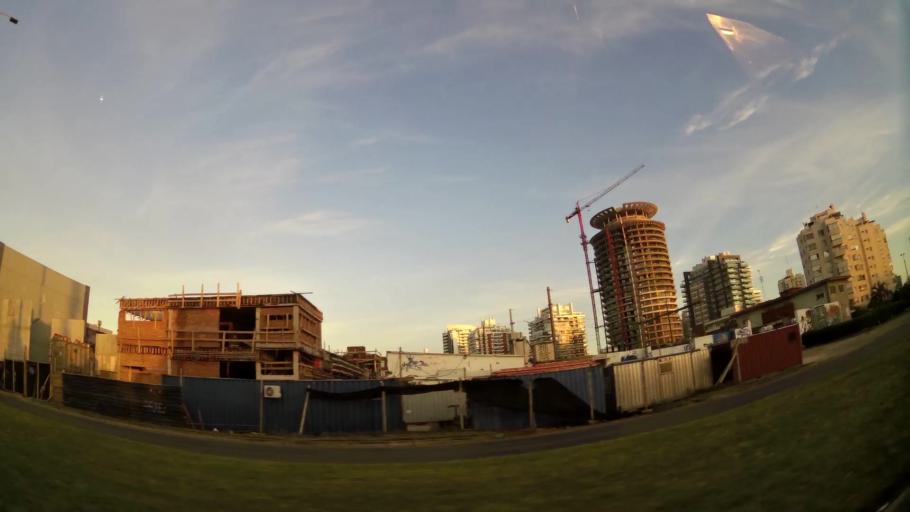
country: UY
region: Maldonado
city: Punta del Este
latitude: -34.9513
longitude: -54.9374
